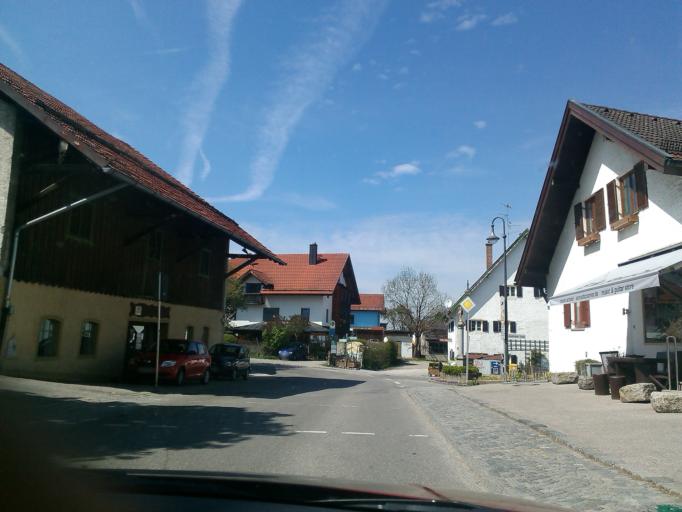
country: DE
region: Bavaria
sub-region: Upper Bavaria
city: Wessling
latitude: 48.0742
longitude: 11.2632
